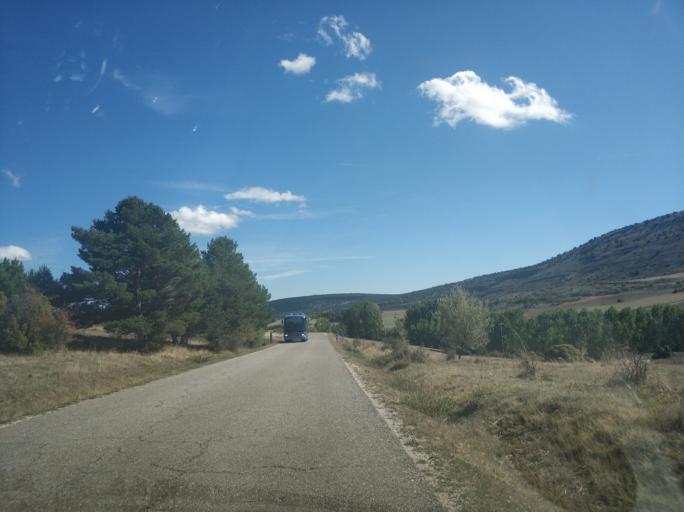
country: ES
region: Castille and Leon
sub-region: Provincia de Burgos
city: Rabanera del Pinar
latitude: 41.8545
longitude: -3.2188
